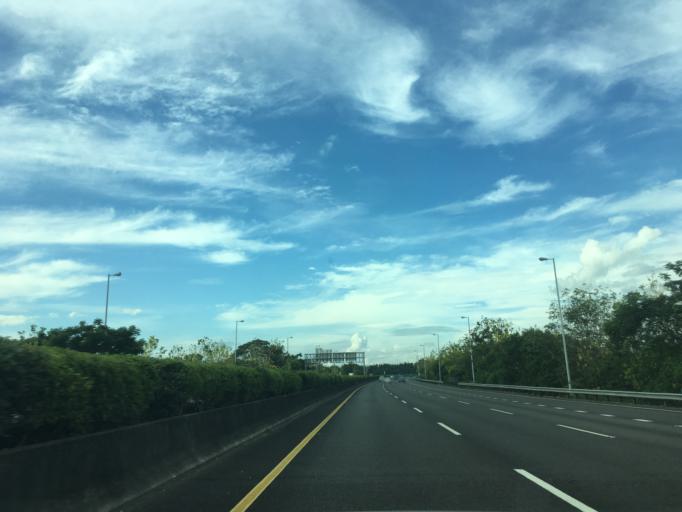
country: TW
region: Taiwan
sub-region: Yunlin
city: Douliu
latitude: 23.5990
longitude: 120.5249
